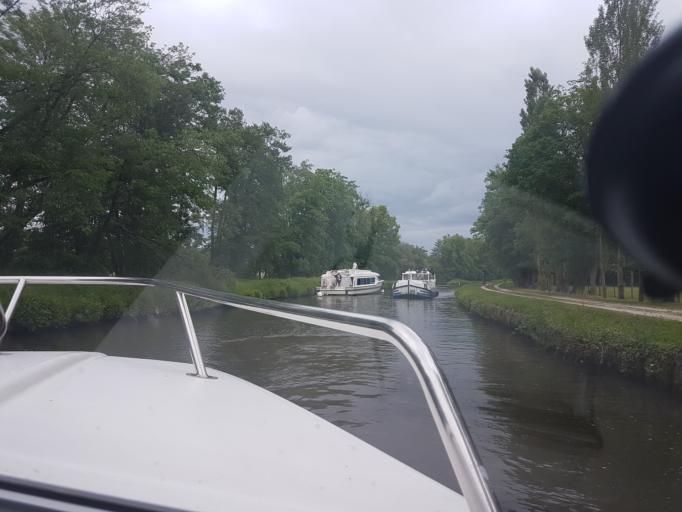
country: FR
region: Bourgogne
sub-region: Departement de l'Yonne
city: Champs-sur-Yonne
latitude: 47.7373
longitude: 3.5946
